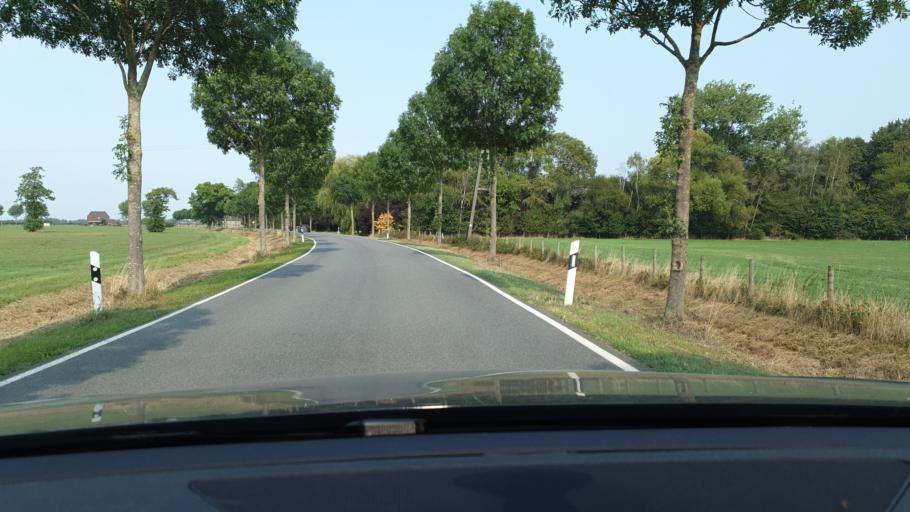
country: DE
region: North Rhine-Westphalia
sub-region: Regierungsbezirk Dusseldorf
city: Kranenburg
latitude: 51.8066
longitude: 6.0144
